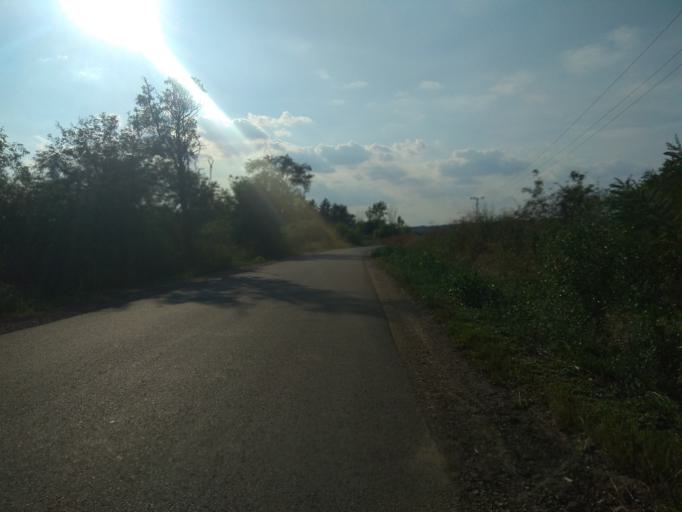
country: HU
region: Borsod-Abauj-Zemplen
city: Harsany
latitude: 47.8963
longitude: 20.7507
